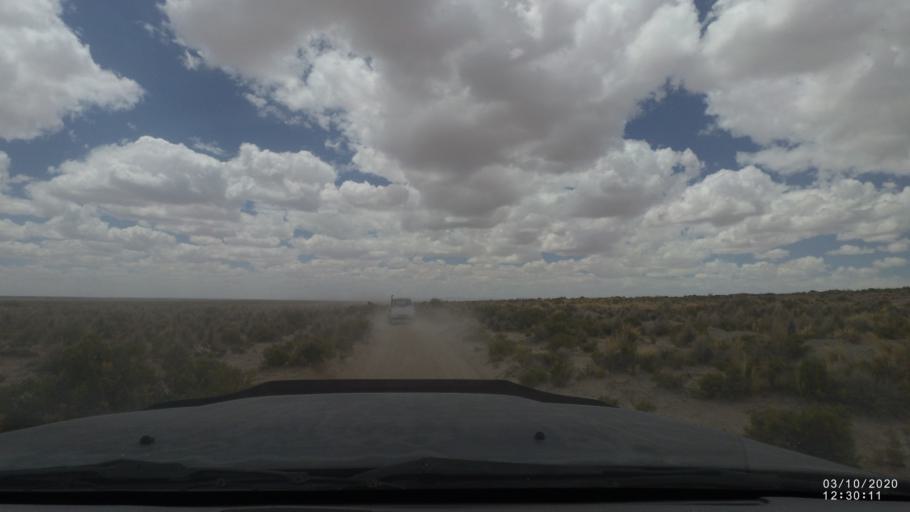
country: BO
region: Oruro
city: Poopo
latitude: -18.6875
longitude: -67.5448
